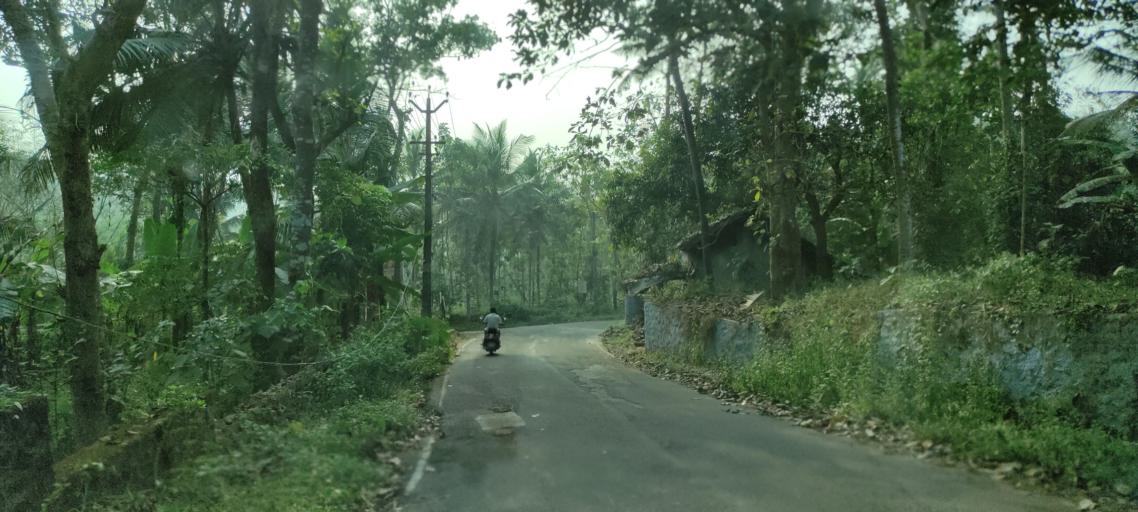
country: IN
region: Kerala
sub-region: Ernakulam
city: Piravam
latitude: 9.8013
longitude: 76.5066
